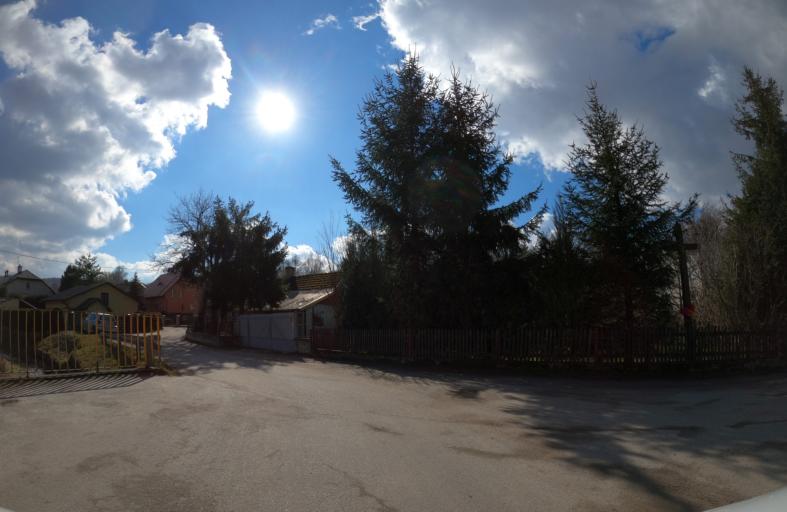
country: PL
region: Subcarpathian Voivodeship
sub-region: Powiat debicki
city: Debica
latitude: 50.0376
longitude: 21.4347
